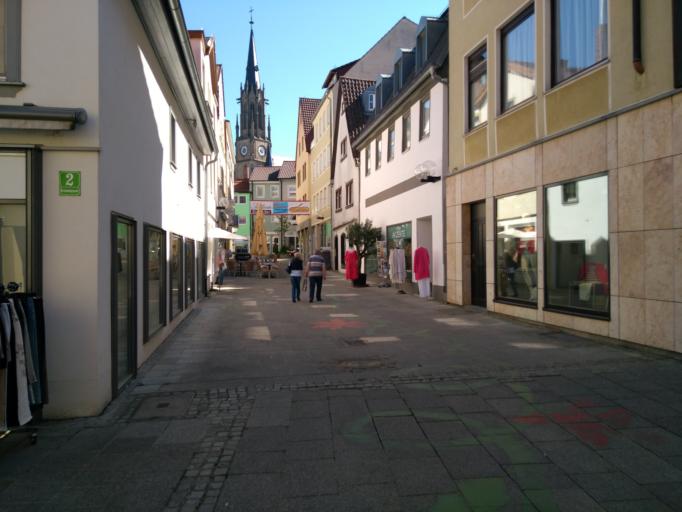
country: DE
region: Bavaria
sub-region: Regierungsbezirk Unterfranken
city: Bad Kissingen
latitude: 50.1998
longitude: 10.0771
